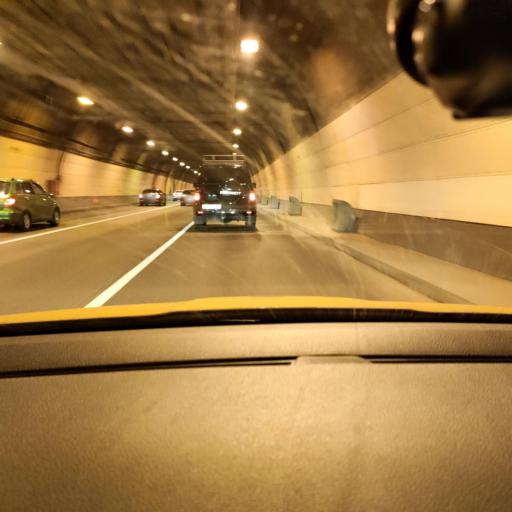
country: RU
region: Moscow
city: Rublevo
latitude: 55.7832
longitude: 37.3926
